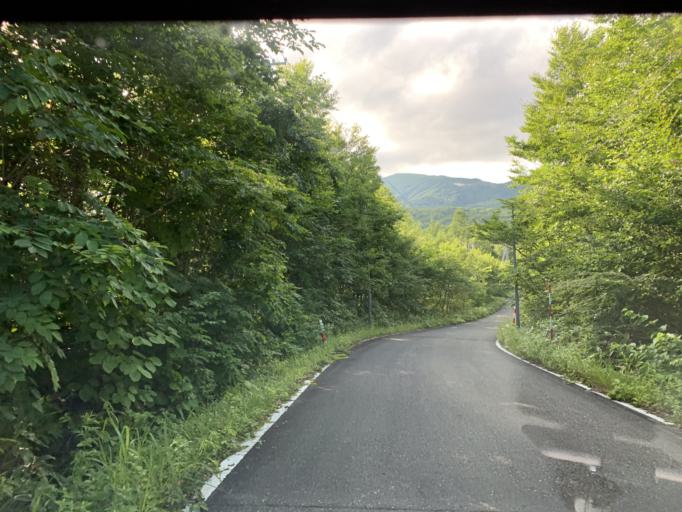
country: JP
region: Iwate
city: Ichinoseki
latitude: 38.9289
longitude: 140.8321
